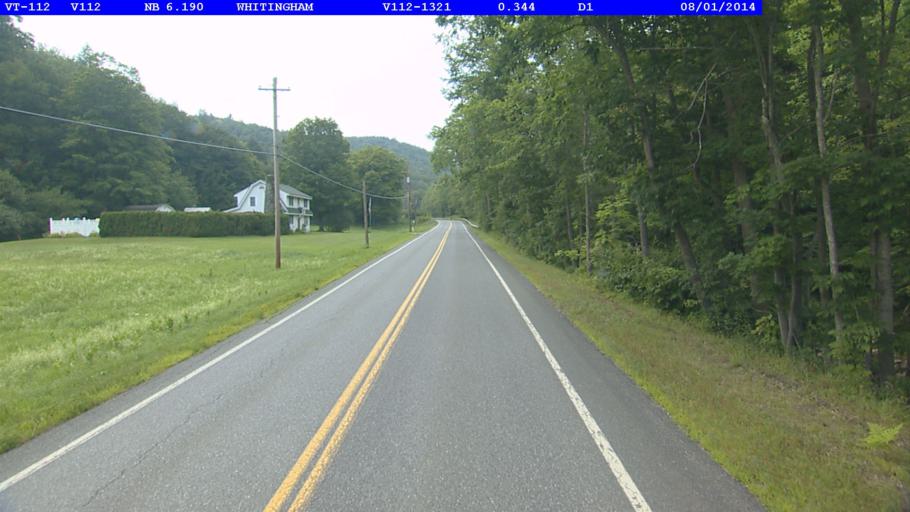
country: US
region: Massachusetts
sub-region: Franklin County
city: Colrain
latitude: 42.7831
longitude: -72.8083
